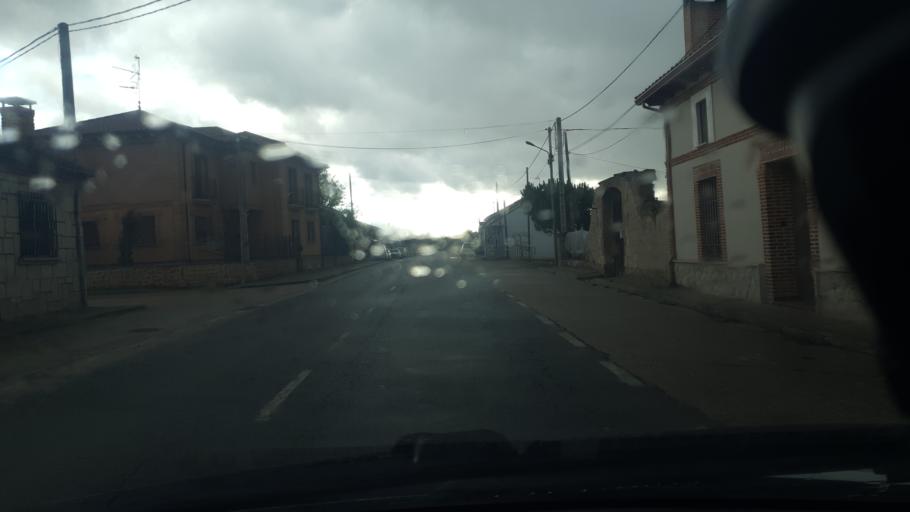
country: ES
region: Castille and Leon
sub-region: Provincia de Segovia
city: Samboal
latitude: 41.2989
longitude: -4.4077
